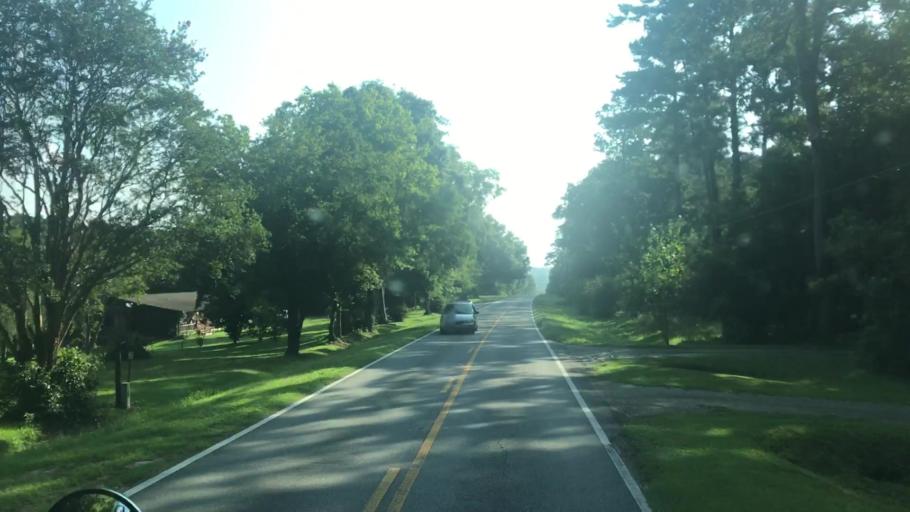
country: US
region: Florida
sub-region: Gadsden County
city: Quincy
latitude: 30.6614
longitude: -84.5602
